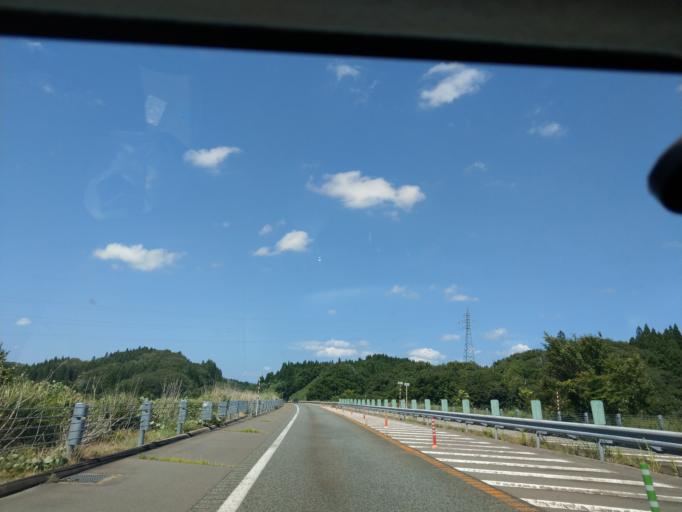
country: JP
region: Akita
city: Akita
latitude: 39.6682
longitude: 140.1883
